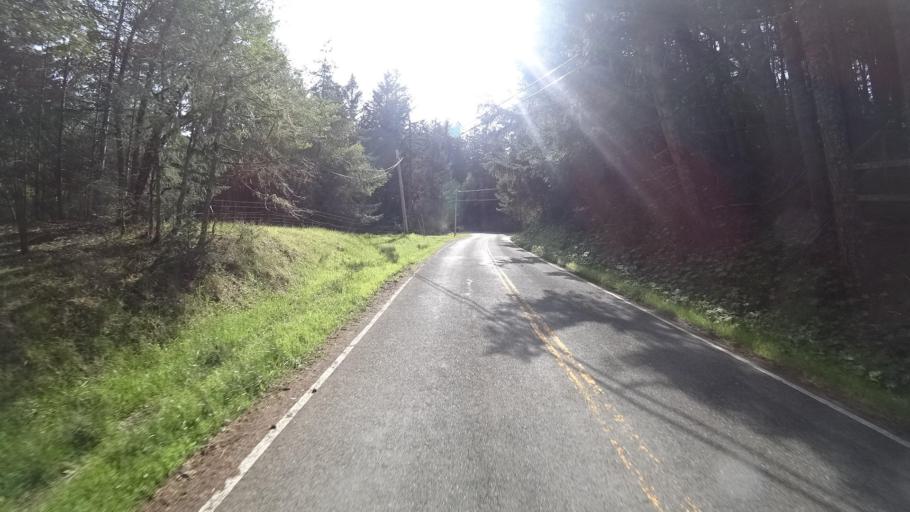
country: US
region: California
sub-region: Humboldt County
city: Blue Lake
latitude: 40.7389
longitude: -123.9555
